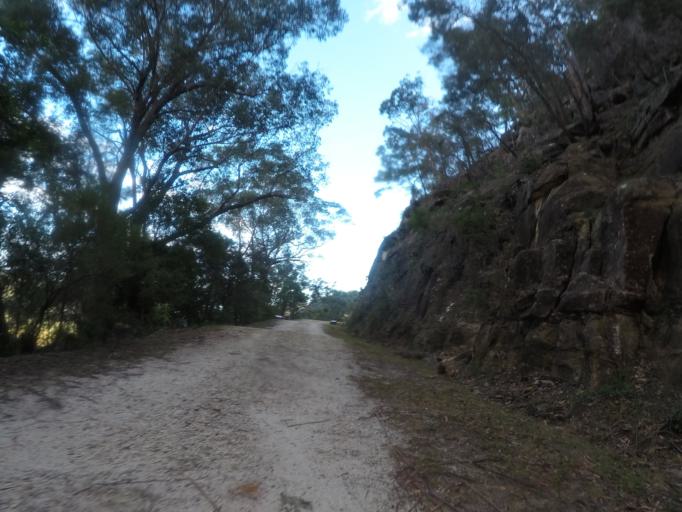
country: AU
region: New South Wales
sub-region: Hornsby Shire
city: Glenorie
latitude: -33.3722
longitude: 150.9848
